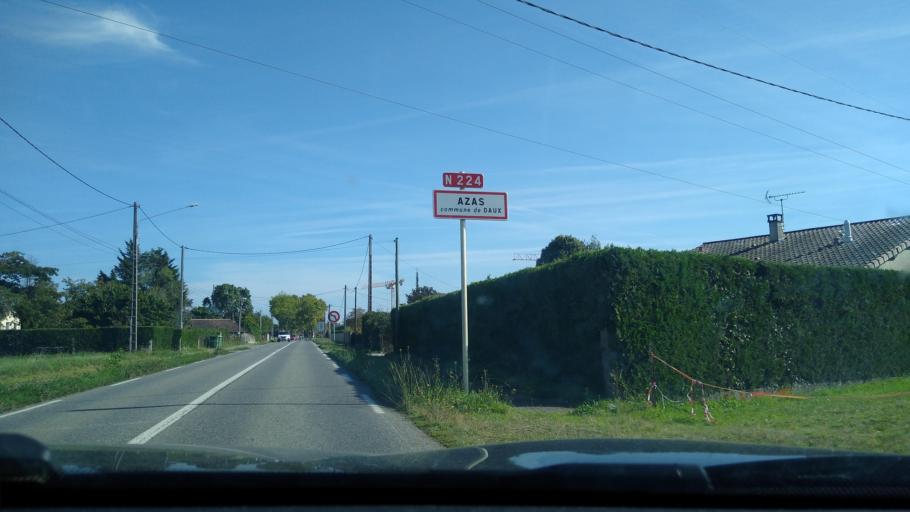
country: FR
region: Midi-Pyrenees
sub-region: Departement de la Haute-Garonne
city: Mondonville
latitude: 43.6749
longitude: 1.2756
